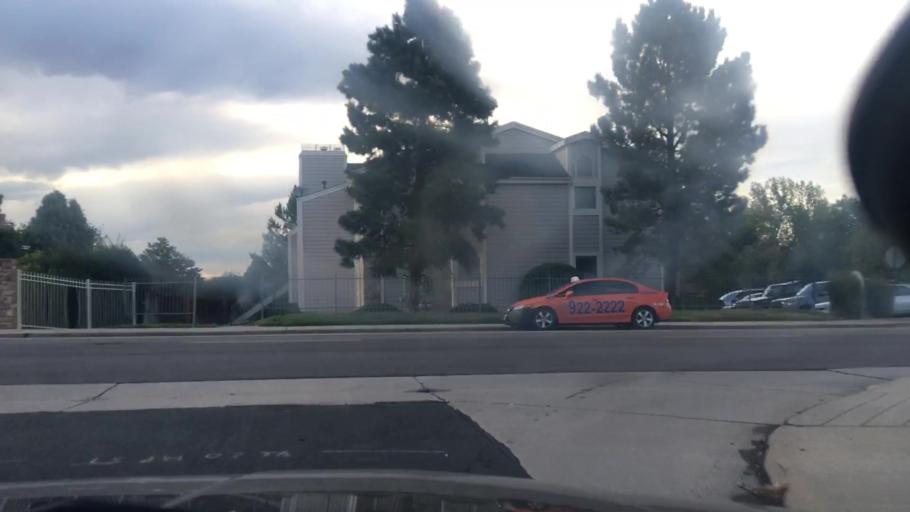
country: US
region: Colorado
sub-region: Arapahoe County
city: Glendale
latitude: 39.6675
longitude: -104.8988
